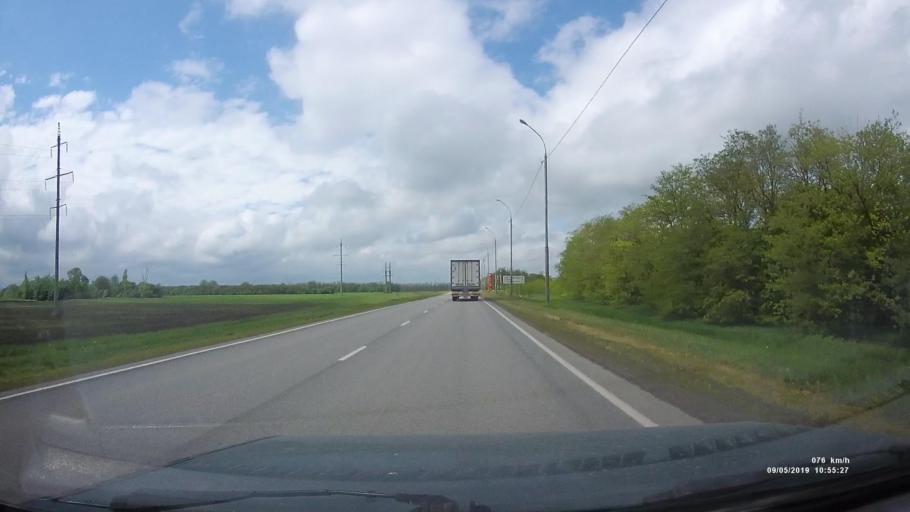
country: RU
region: Rostov
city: Peshkovo
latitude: 46.8728
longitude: 39.3151
